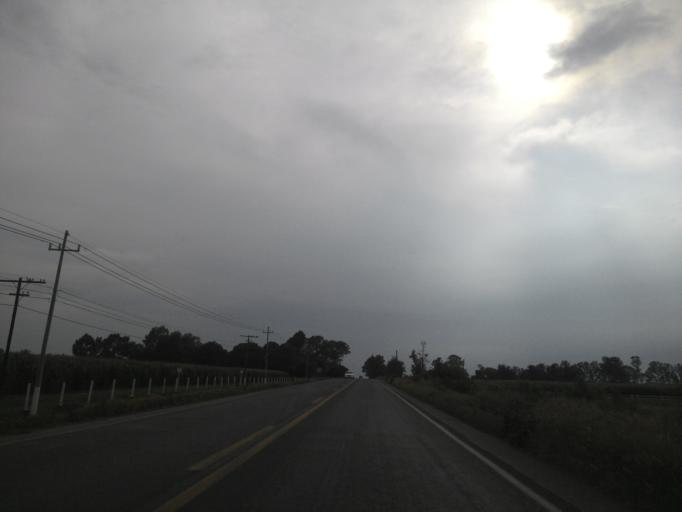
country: MX
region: Jalisco
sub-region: Acatic
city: Tierras Coloradas
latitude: 20.7271
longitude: -102.8819
